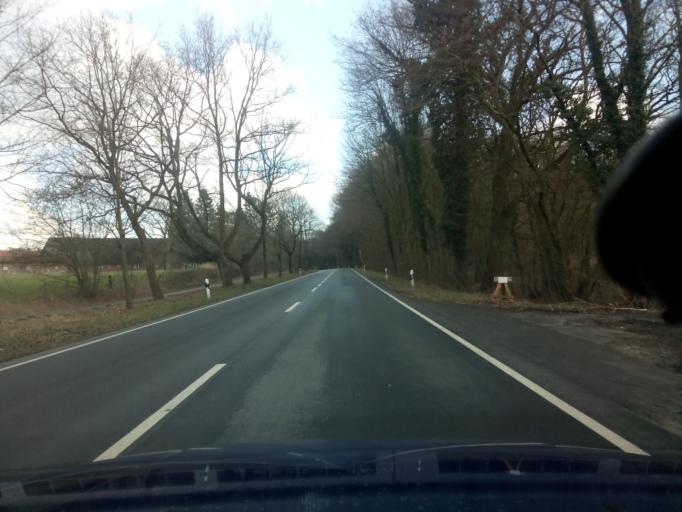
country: DE
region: Lower Saxony
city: Vollersode
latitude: 53.3577
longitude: 8.9275
